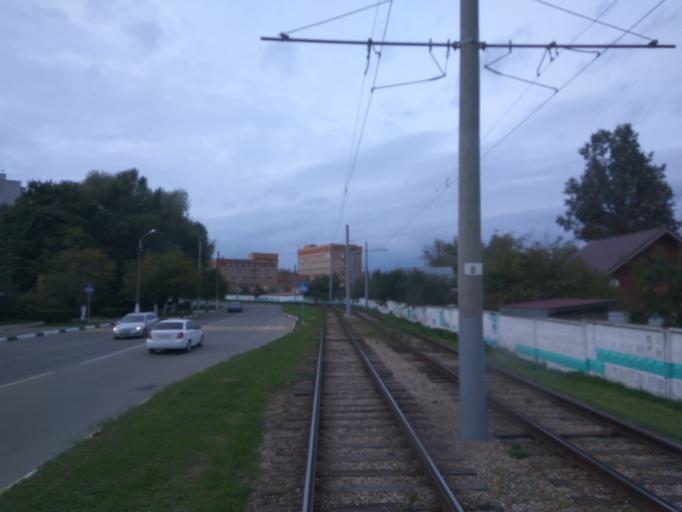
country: RU
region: Moskovskaya
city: Kolomna
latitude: 55.0646
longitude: 38.7565
